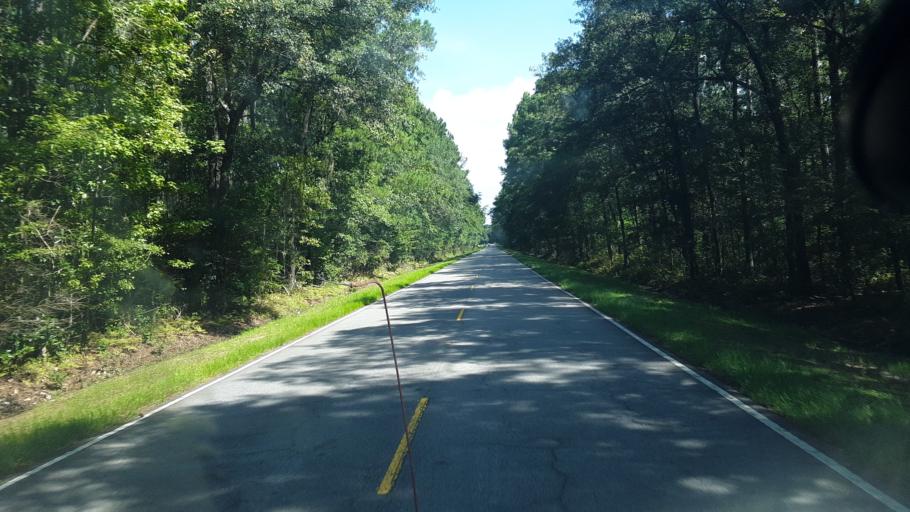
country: US
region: South Carolina
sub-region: Hampton County
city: Hampton
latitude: 33.0074
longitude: -81.0459
